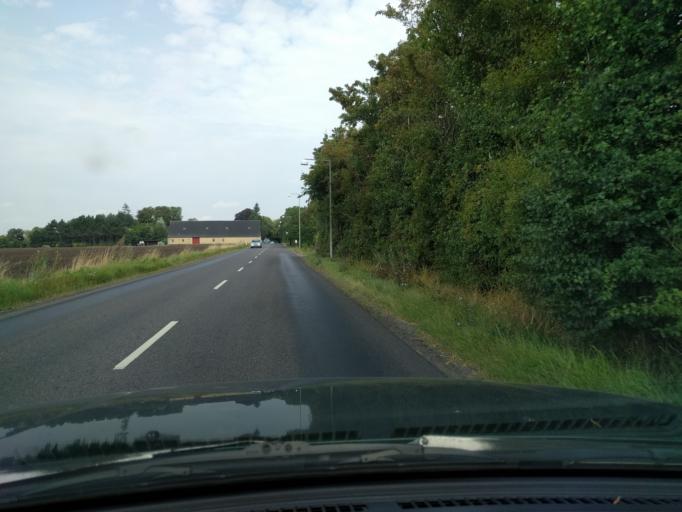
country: DK
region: South Denmark
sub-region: Odense Kommune
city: Neder Holluf
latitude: 55.3944
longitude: 10.4630
